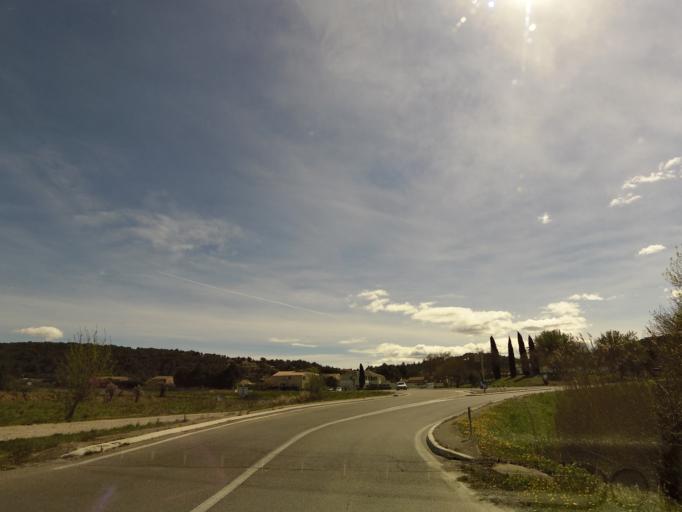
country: FR
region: Languedoc-Roussillon
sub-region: Departement du Gard
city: Langlade
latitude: 43.8107
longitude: 4.2448
